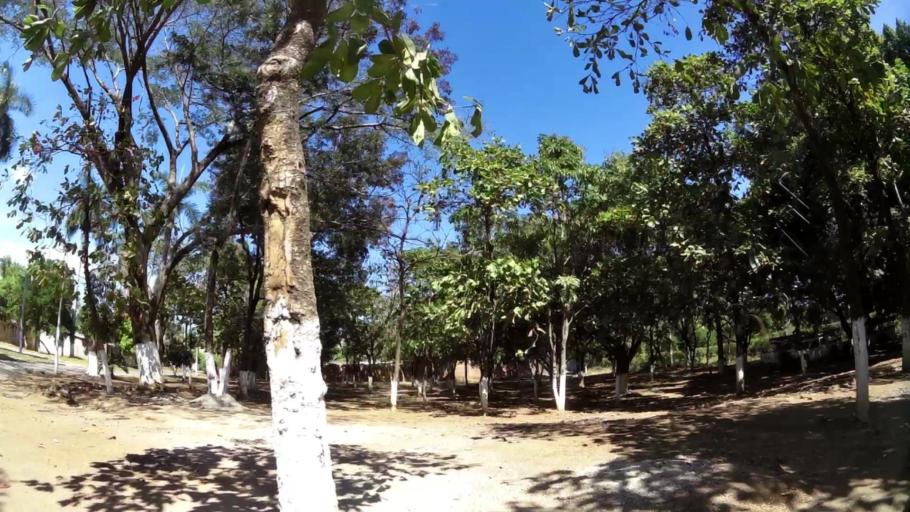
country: SV
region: Ahuachapan
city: Atiquizaya
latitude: 13.9698
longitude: -89.7581
